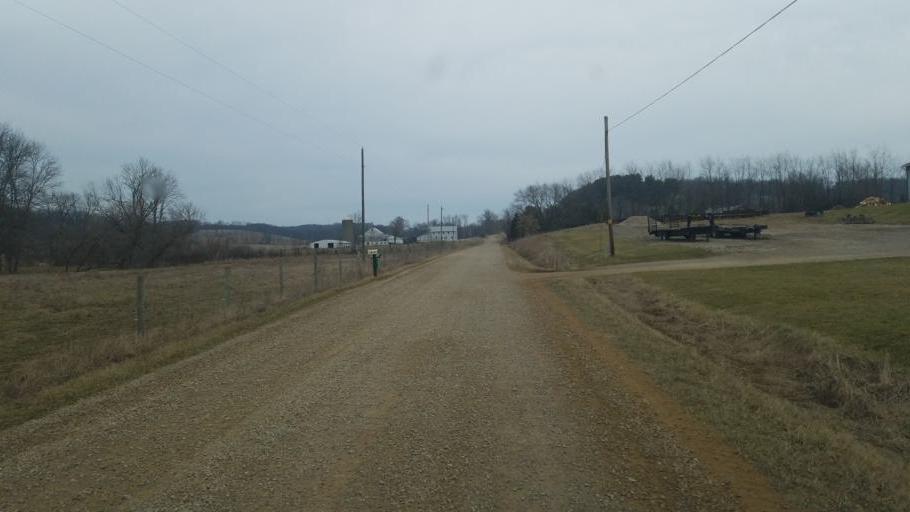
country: US
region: Ohio
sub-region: Knox County
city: Danville
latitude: 40.5109
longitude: -82.2865
